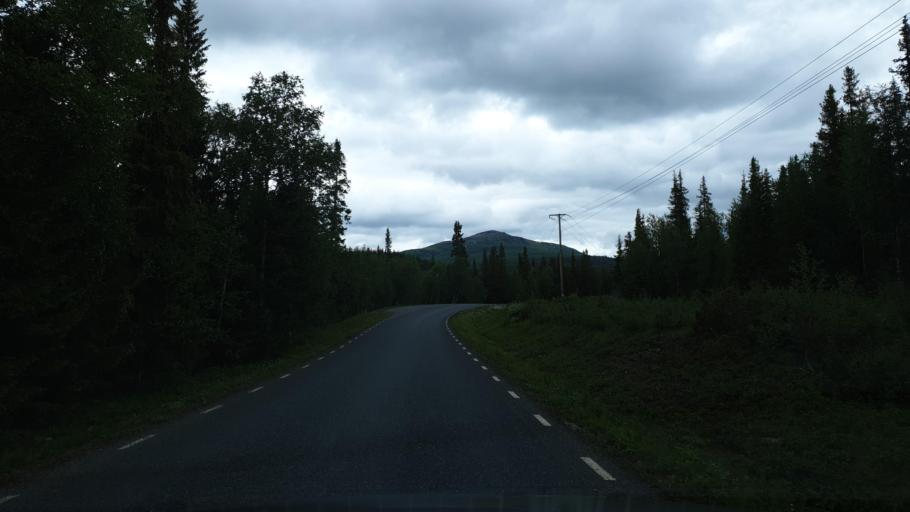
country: SE
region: Vaesterbotten
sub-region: Vilhelmina Kommun
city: Sjoberg
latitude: 65.2695
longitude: 15.3689
